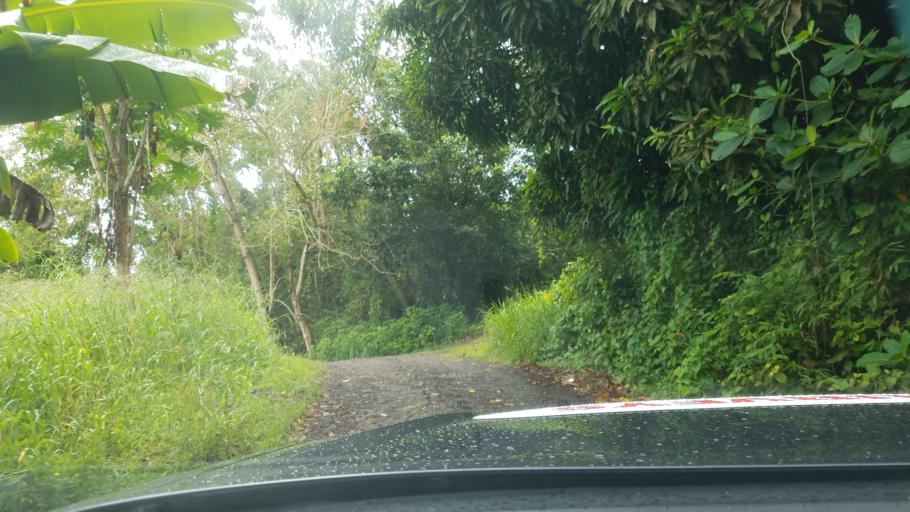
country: LC
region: Castries Quarter
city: Bisee
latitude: 13.9990
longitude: -60.9585
